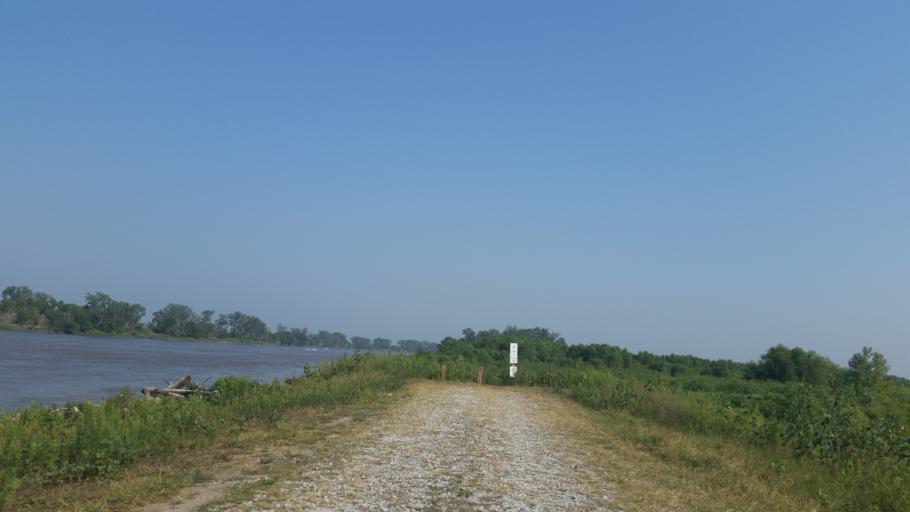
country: US
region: Nebraska
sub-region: Cass County
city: Plattsmouth
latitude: 41.0511
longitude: -95.8812
